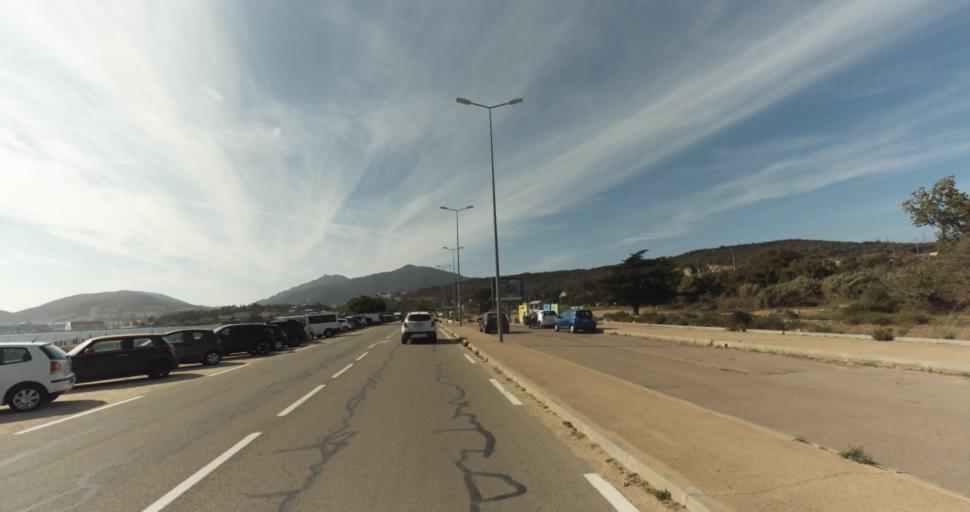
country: FR
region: Corsica
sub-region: Departement de la Corse-du-Sud
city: Ajaccio
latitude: 41.9254
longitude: 8.7808
